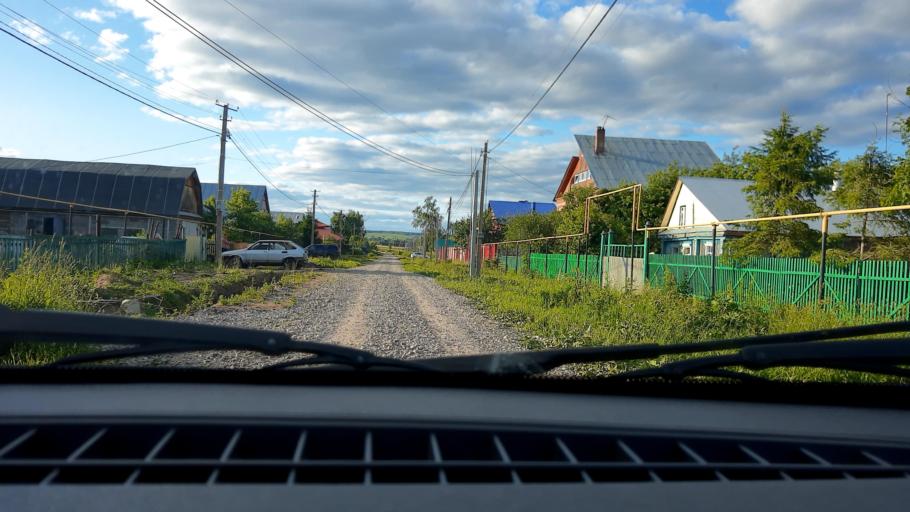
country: RU
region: Bashkortostan
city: Mikhaylovka
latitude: 54.8829
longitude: 55.8775
